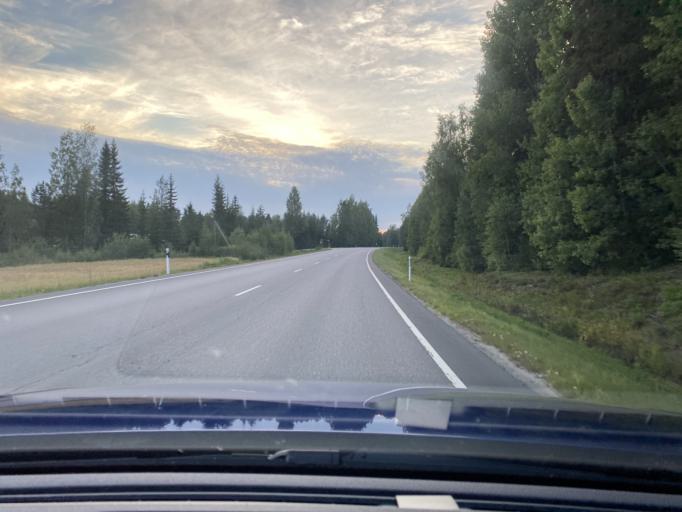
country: FI
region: Satakunta
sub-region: Pohjois-Satakunta
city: Kankaanpaeae
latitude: 61.7813
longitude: 22.4387
